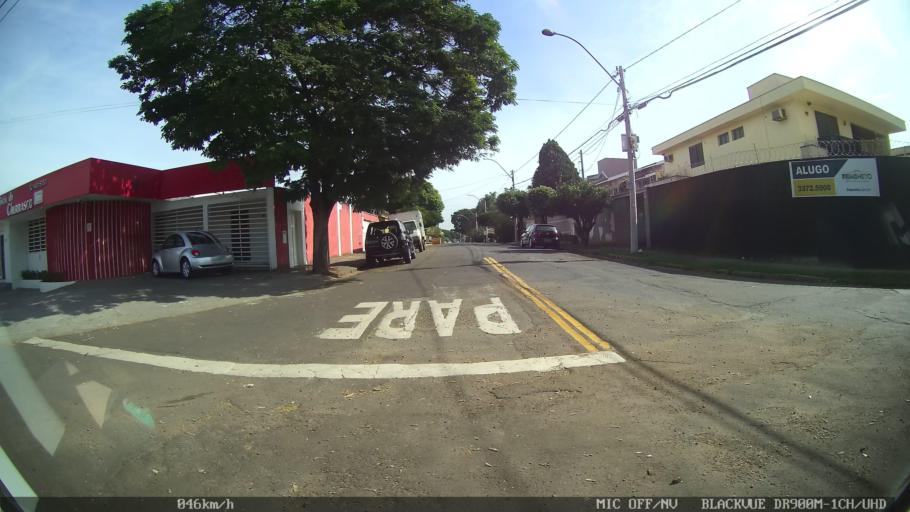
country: BR
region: Sao Paulo
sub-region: Piracicaba
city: Piracicaba
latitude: -22.7209
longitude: -47.6638
